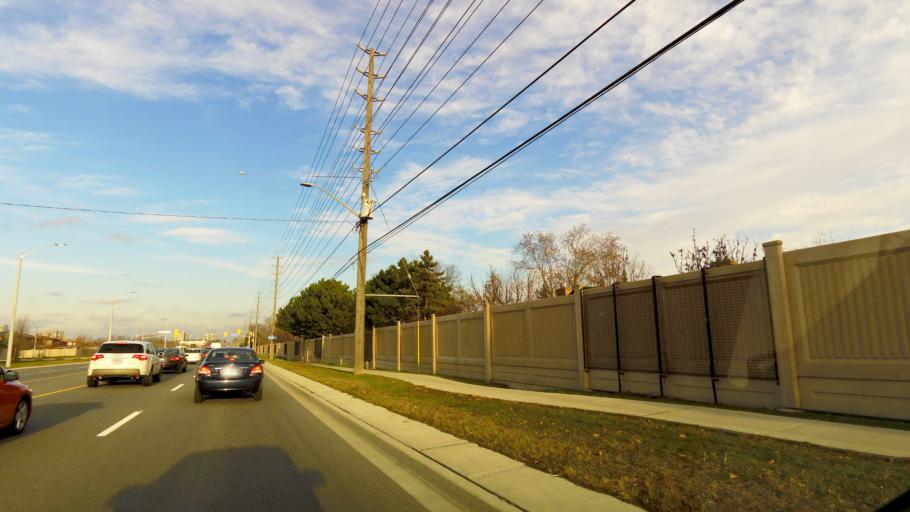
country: CA
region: Ontario
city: Mississauga
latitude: 43.6106
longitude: -79.6157
